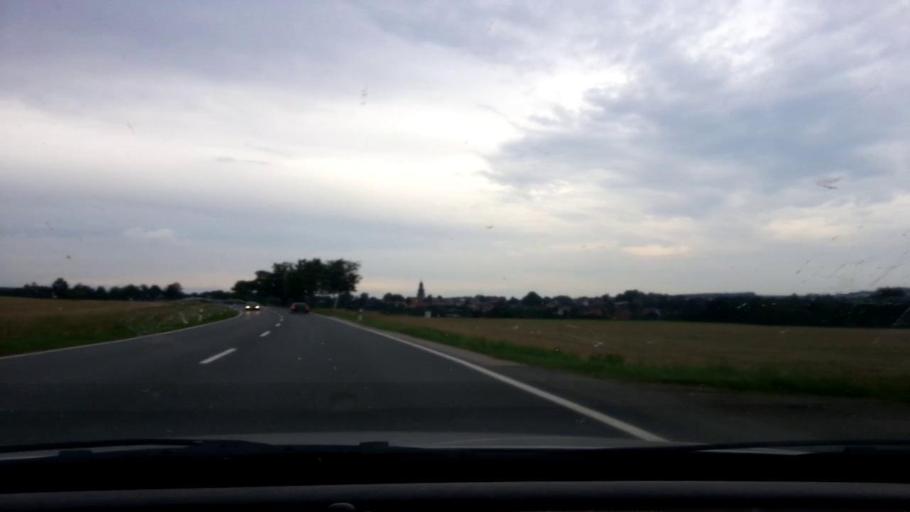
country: DE
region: Bavaria
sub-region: Upper Franconia
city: Neunkirchen am Main
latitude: 49.9154
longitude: 11.6532
